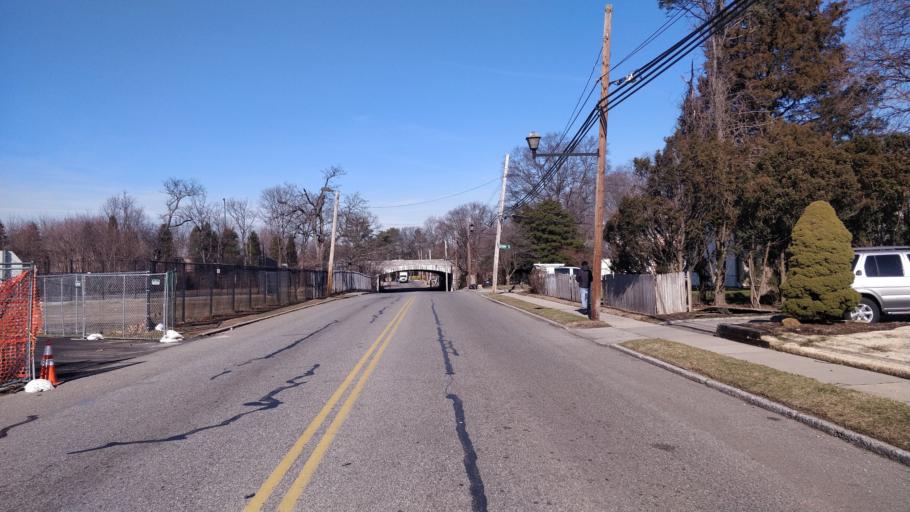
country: US
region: New York
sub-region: Nassau County
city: Westbury
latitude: 40.7637
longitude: -73.5817
